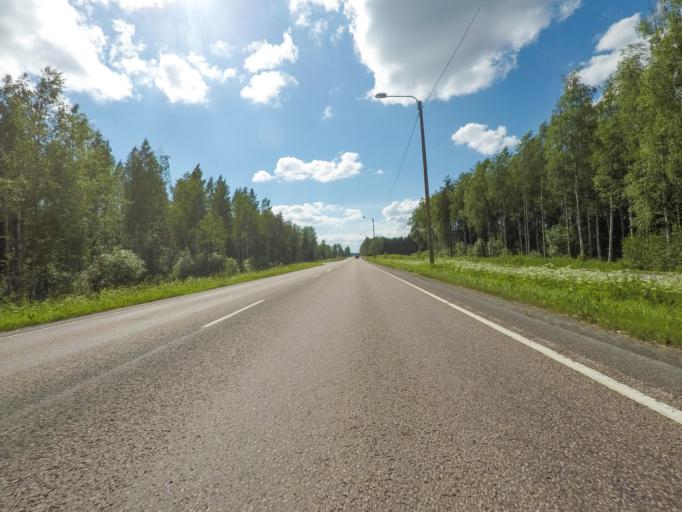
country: FI
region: Southern Savonia
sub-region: Savonlinna
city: Savonlinna
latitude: 61.8828
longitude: 29.0711
